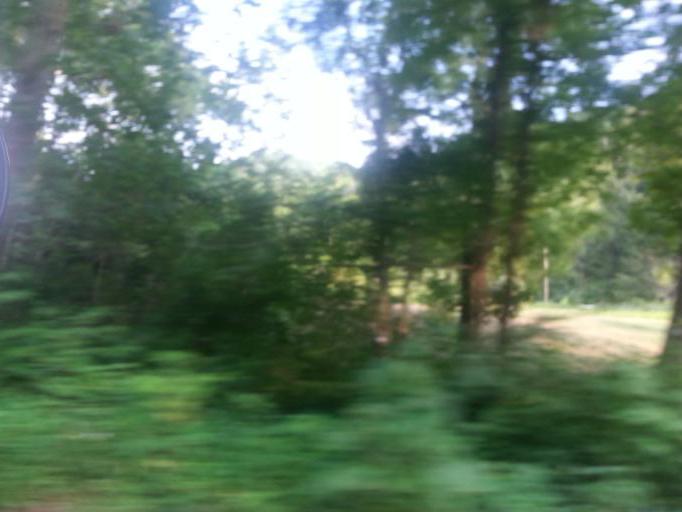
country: US
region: Tennessee
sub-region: Morgan County
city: Coalfield
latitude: 36.1259
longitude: -84.4173
